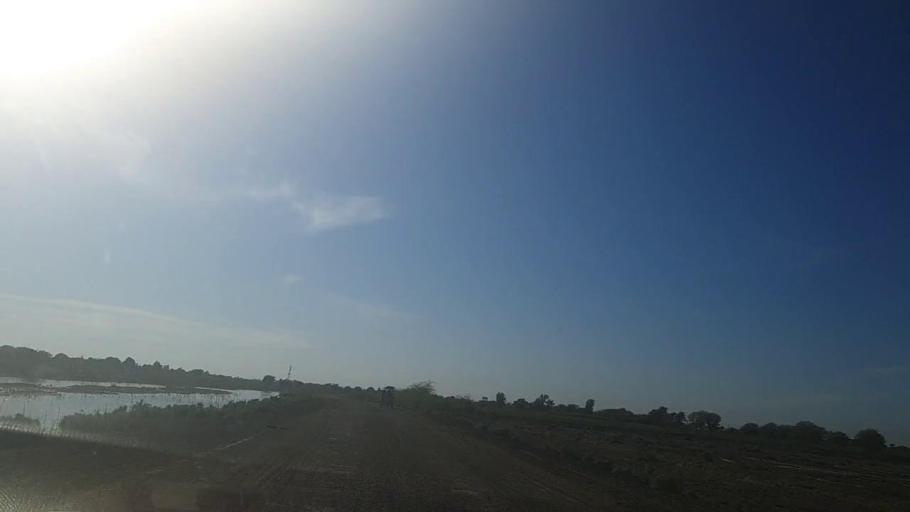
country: PK
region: Sindh
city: Pithoro
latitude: 25.5111
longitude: 69.3969
